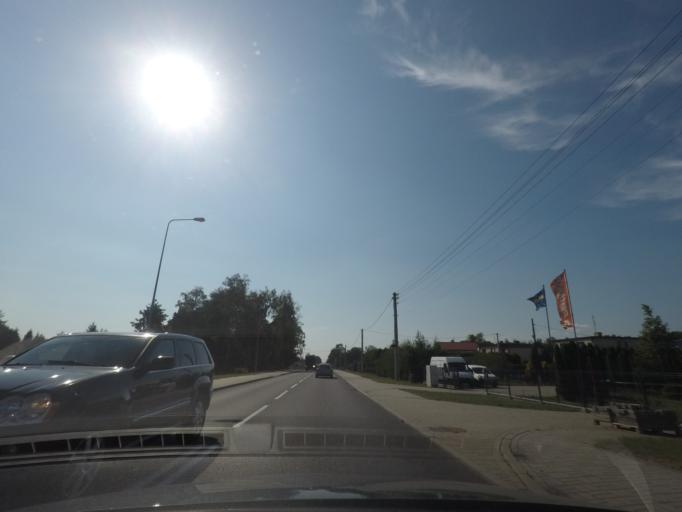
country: PL
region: Silesian Voivodeship
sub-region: Powiat pszczynski
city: Rudziczka
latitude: 50.0382
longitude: 18.7458
